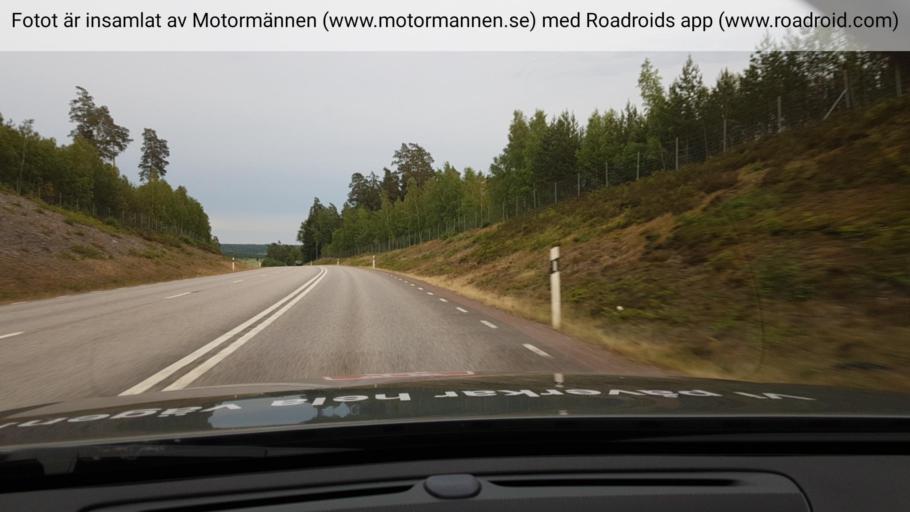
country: SE
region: OEstergoetland
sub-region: Motala Kommun
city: Borensberg
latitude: 58.5647
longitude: 15.3059
